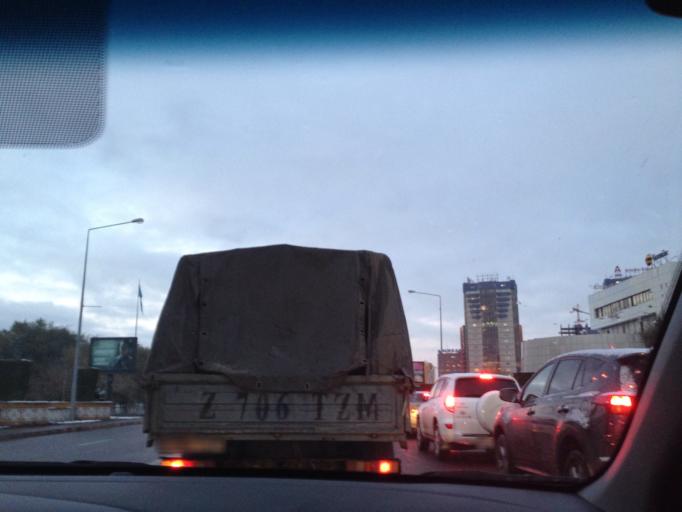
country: KZ
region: Astana Qalasy
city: Astana
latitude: 51.1432
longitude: 71.4201
